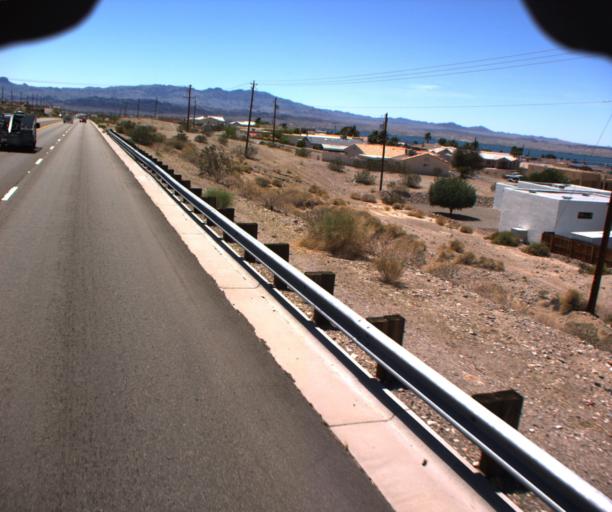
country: US
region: Arizona
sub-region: Mohave County
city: Lake Havasu City
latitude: 34.5137
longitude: -114.3496
